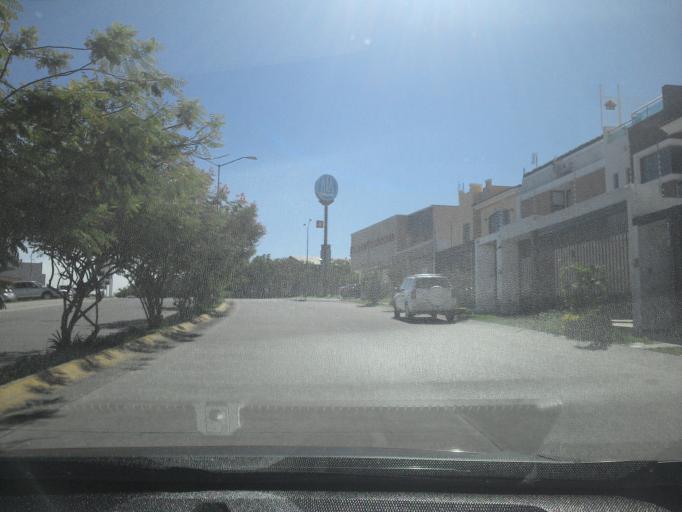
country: MX
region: Jalisco
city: Nuevo Mexico
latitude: 20.7513
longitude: -103.4133
